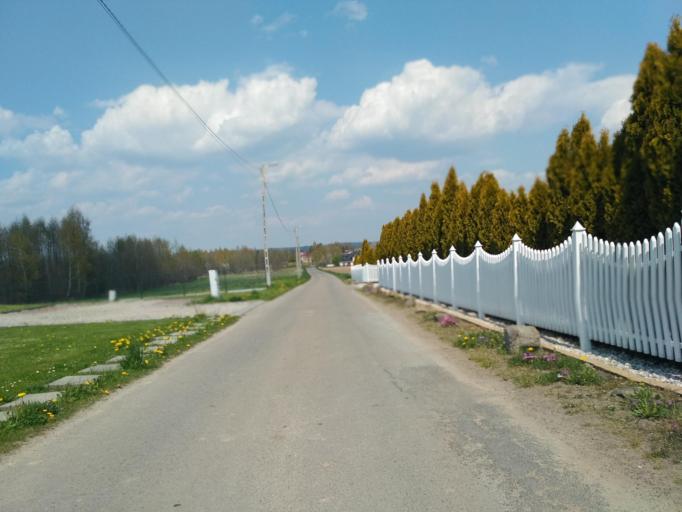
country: PL
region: Subcarpathian Voivodeship
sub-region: Powiat jasielski
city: Jaslo
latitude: 49.7182
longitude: 21.5123
